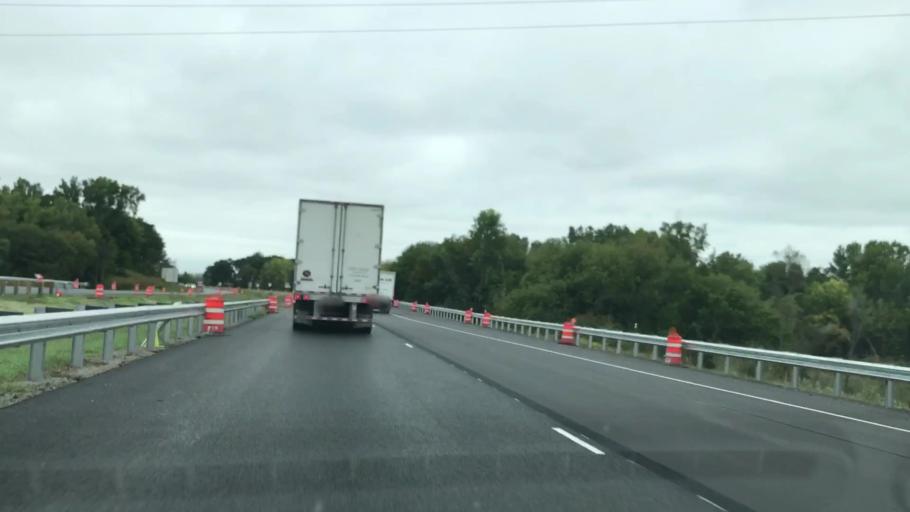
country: US
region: Wisconsin
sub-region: Brown County
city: Suamico
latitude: 44.6310
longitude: -88.0483
